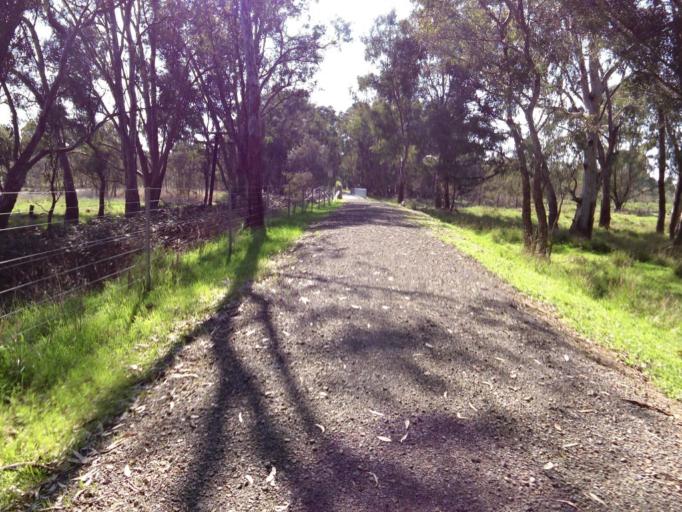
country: AU
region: Victoria
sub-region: Murrindindi
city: Alexandra
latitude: -37.1555
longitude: 145.5743
